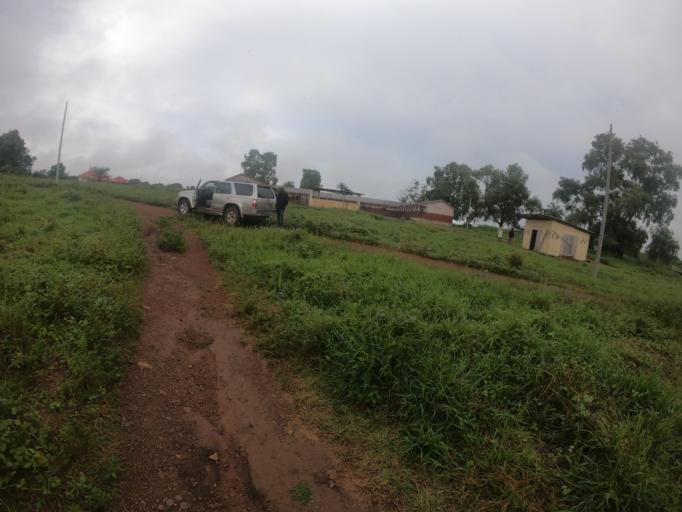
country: SL
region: Northern Province
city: Port Loko
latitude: 8.4951
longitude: -12.7506
